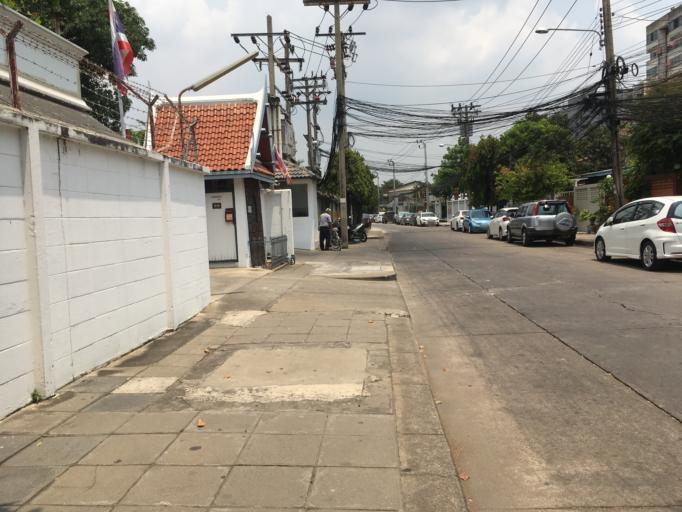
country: TH
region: Bangkok
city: Phaya Thai
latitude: 13.7918
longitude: 100.5448
